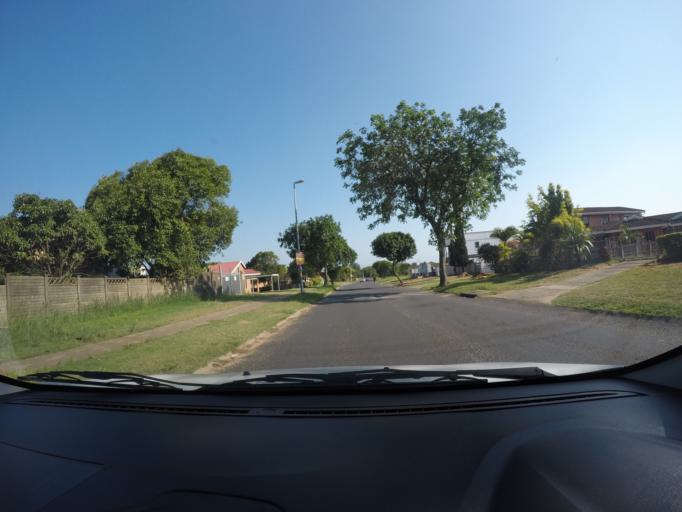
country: ZA
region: KwaZulu-Natal
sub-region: uThungulu District Municipality
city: Richards Bay
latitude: -28.7246
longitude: 32.0417
